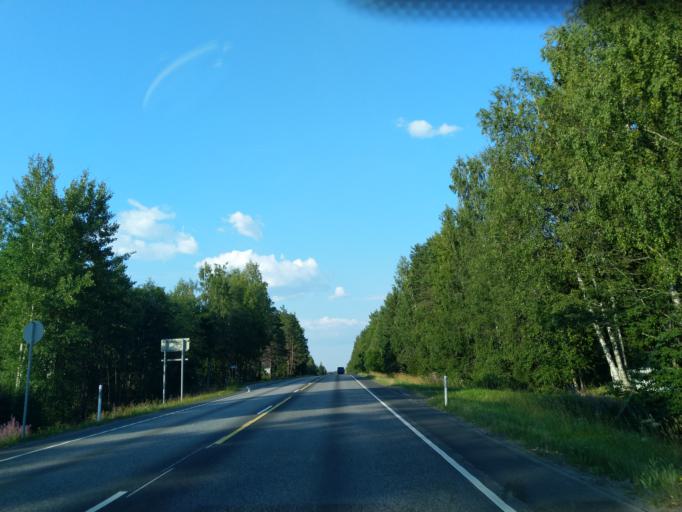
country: FI
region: Satakunta
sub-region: Pori
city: Pomarkku
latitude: 61.7033
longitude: 22.0179
